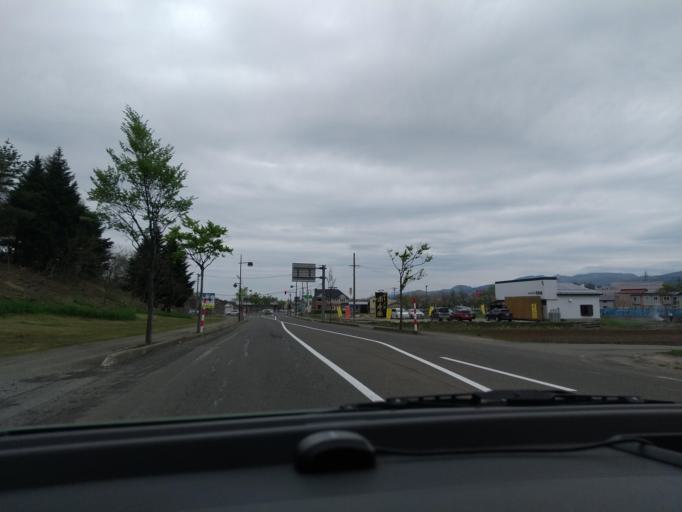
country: JP
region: Akita
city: Yokotemachi
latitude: 39.2925
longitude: 140.5496
